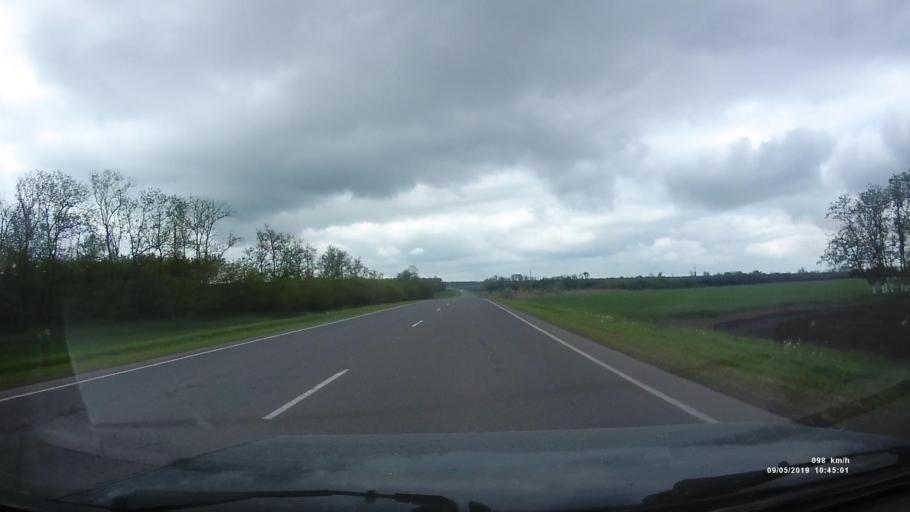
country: RU
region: Rostov
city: Peshkovo
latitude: 46.9980
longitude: 39.3762
